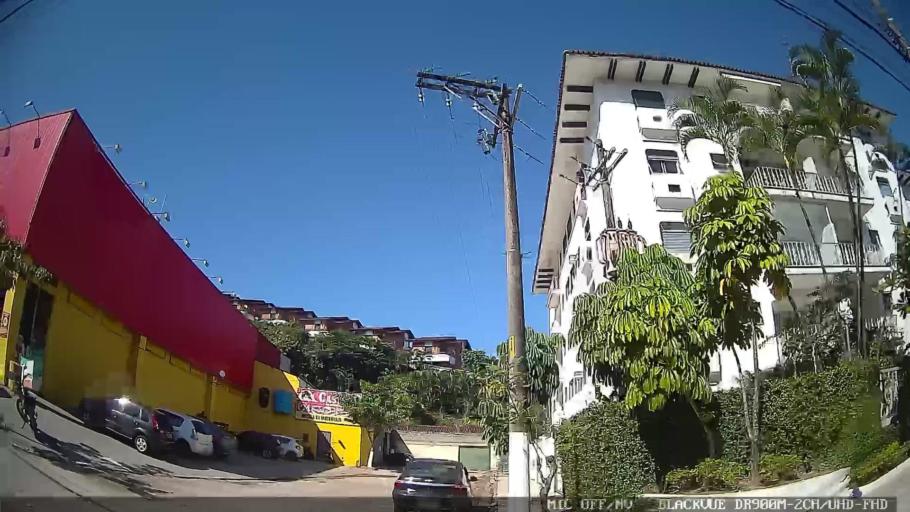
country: BR
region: Sao Paulo
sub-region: Guaruja
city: Guaruja
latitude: -23.9906
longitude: -46.2407
